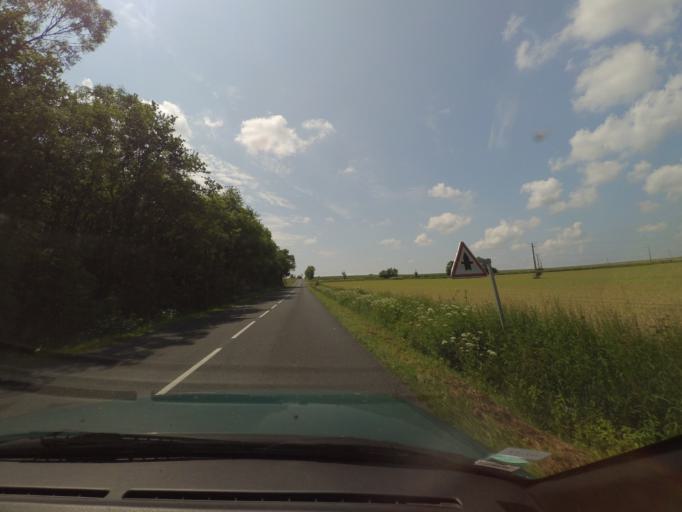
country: FR
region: Pays de la Loire
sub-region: Departement de la Vendee
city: Saint-Hilaire-de-Loulay
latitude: 47.0306
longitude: -1.3290
